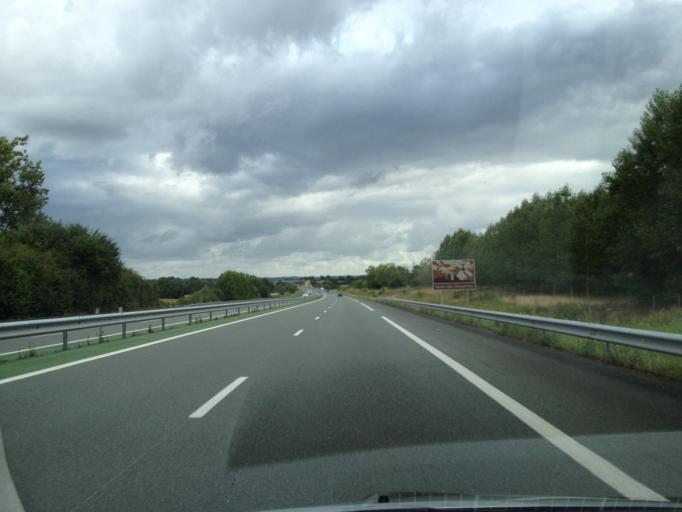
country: FR
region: Pays de la Loire
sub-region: Departement de la Vendee
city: Vendrennes
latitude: 46.8681
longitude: -1.1285
